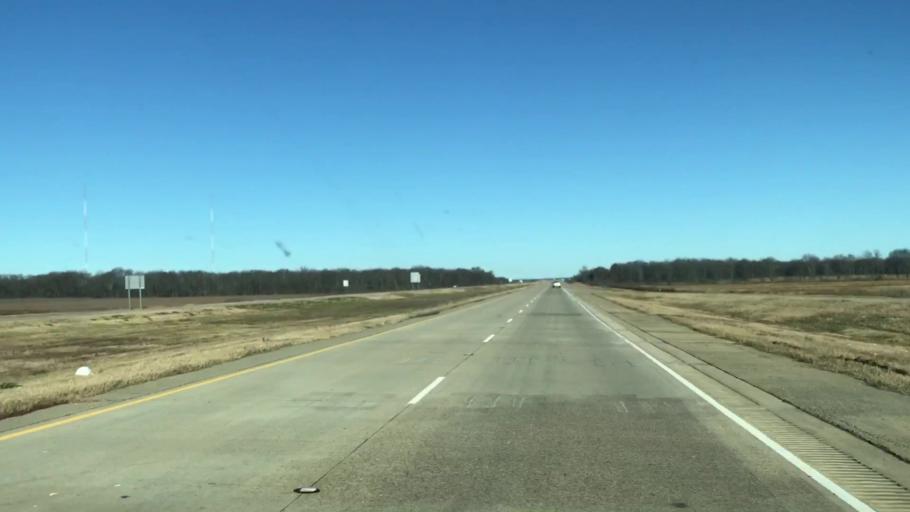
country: US
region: Louisiana
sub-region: Caddo Parish
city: Blanchard
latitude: 32.6782
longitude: -93.8514
